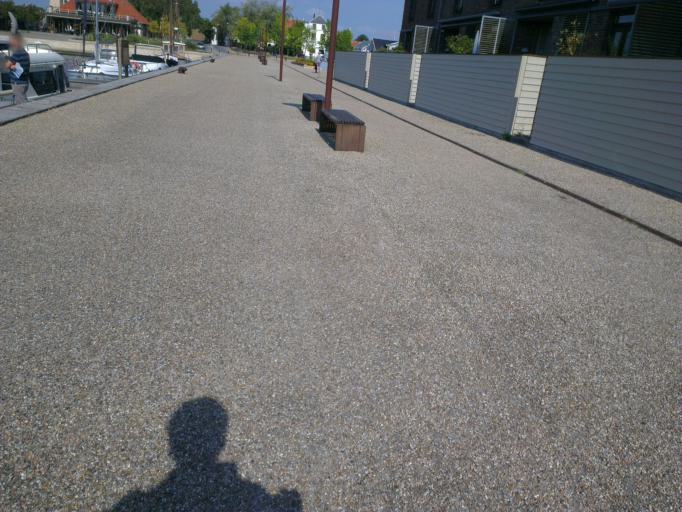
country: DK
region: Capital Region
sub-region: Frederikssund Kommune
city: Frederikssund
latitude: 55.8358
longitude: 12.0563
